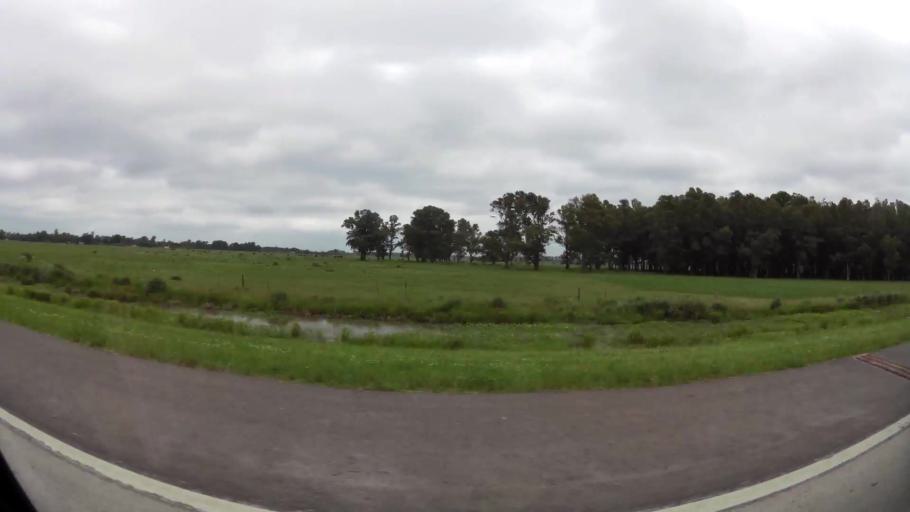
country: AR
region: Buenos Aires
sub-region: Partido de Brandsen
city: Brandsen
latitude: -35.0486
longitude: -58.1298
